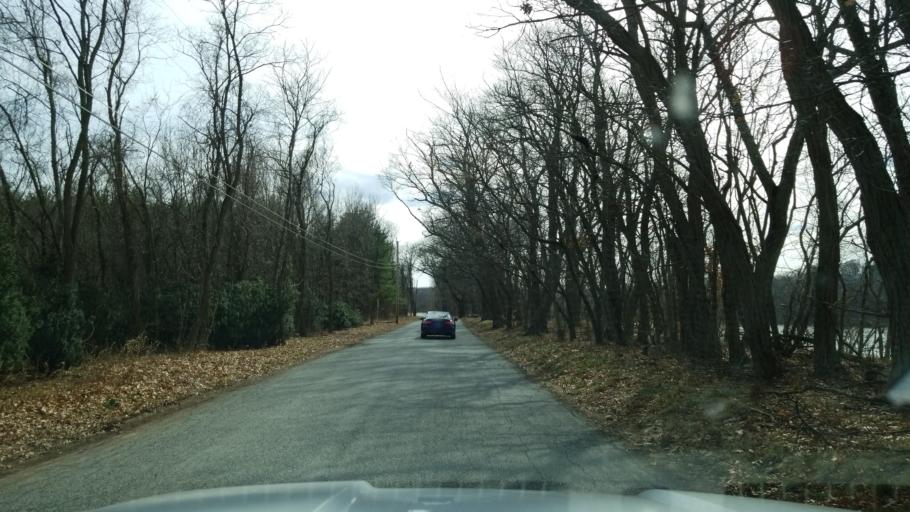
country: US
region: Connecticut
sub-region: Middlesex County
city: Cromwell
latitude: 41.6395
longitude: -72.6257
